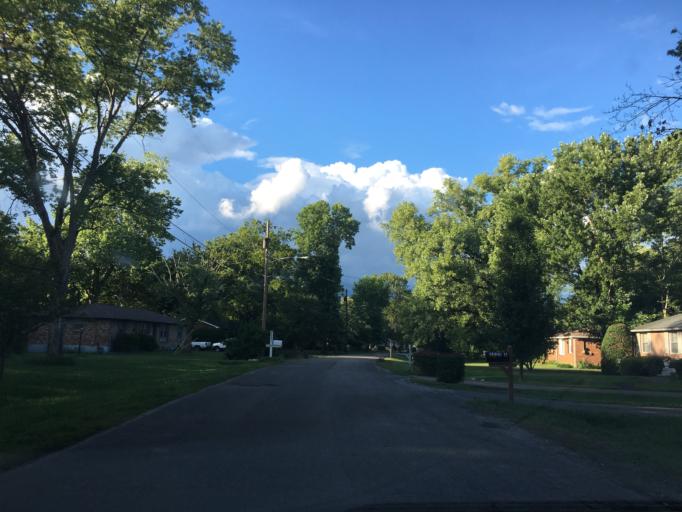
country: US
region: Tennessee
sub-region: Davidson County
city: Oak Hill
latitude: 36.0684
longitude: -86.7381
